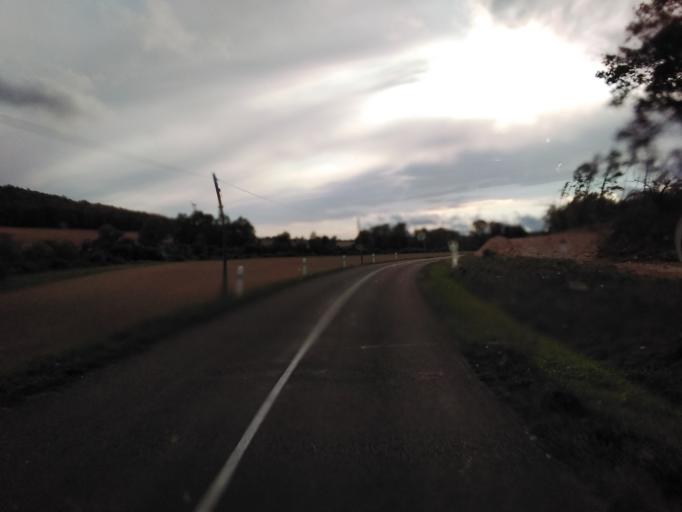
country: FR
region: Champagne-Ardenne
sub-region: Departement de l'Aube
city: Les Riceys
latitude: 47.9455
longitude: 4.3741
